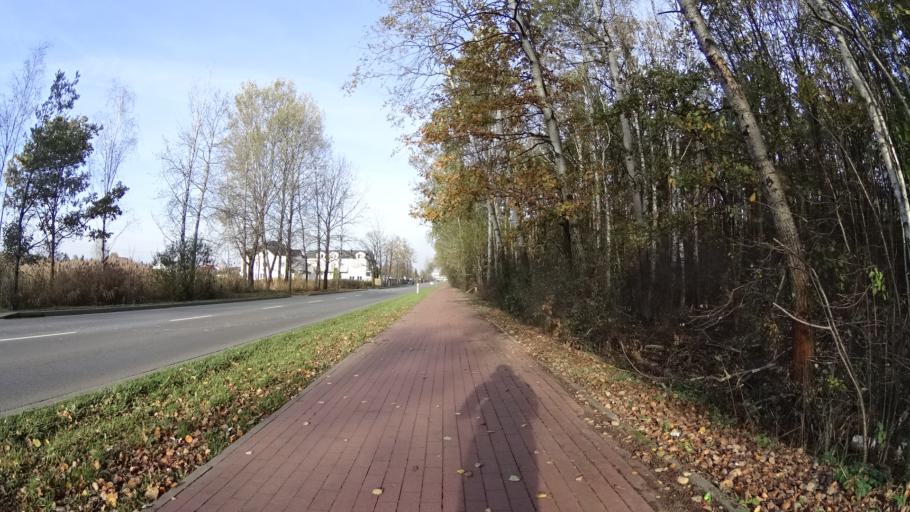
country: PL
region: Masovian Voivodeship
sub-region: Powiat warszawski zachodni
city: Babice
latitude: 52.2713
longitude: 20.8625
